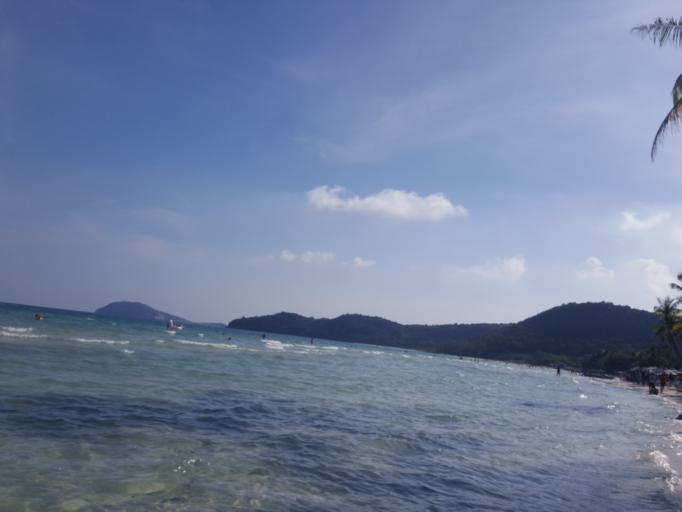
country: VN
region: Kien Giang
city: Duong GJong
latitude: 10.0592
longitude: 104.0375
